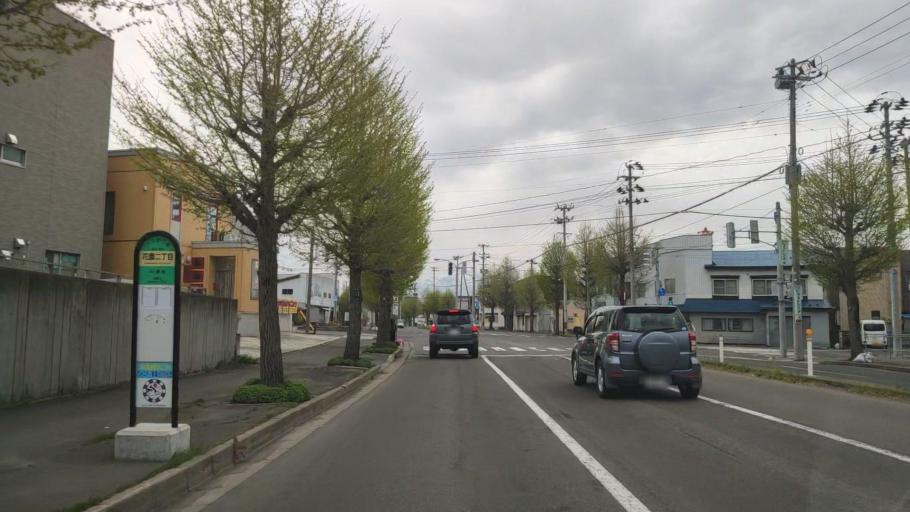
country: JP
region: Aomori
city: Aomori Shi
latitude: 40.8222
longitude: 140.7704
